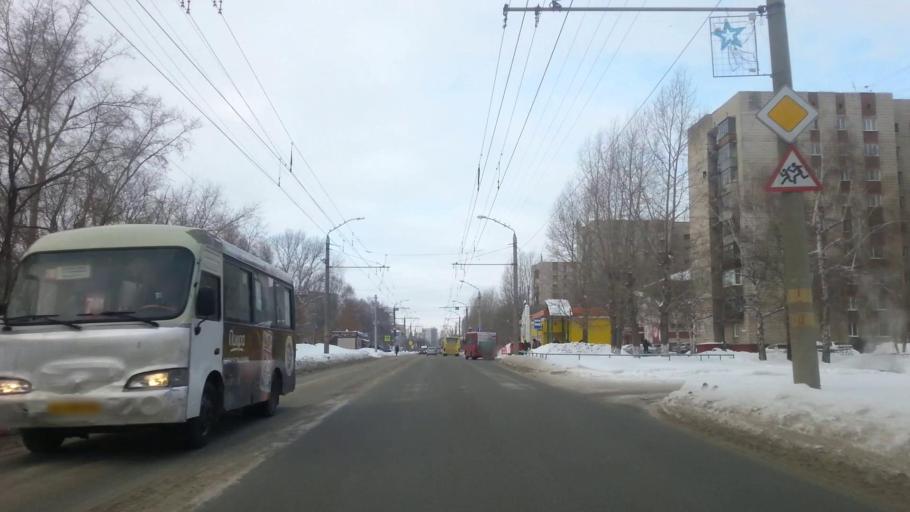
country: RU
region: Altai Krai
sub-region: Gorod Barnaulskiy
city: Barnaul
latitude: 53.3694
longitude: 83.6982
